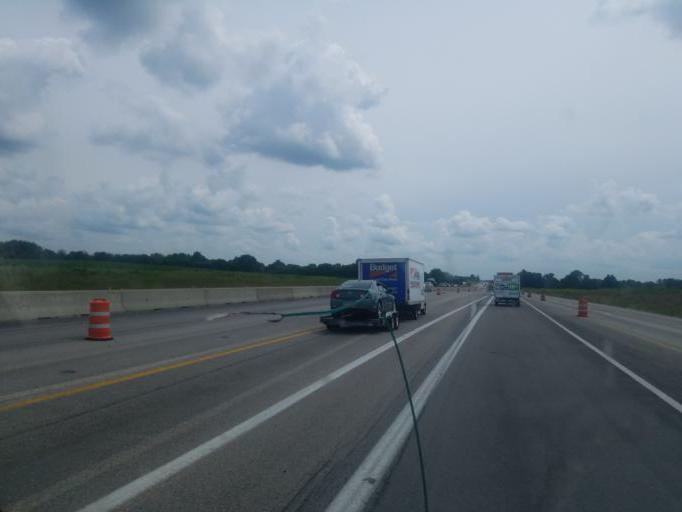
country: US
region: Kentucky
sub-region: Larue County
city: Hodgenville
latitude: 37.5508
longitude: -85.8782
